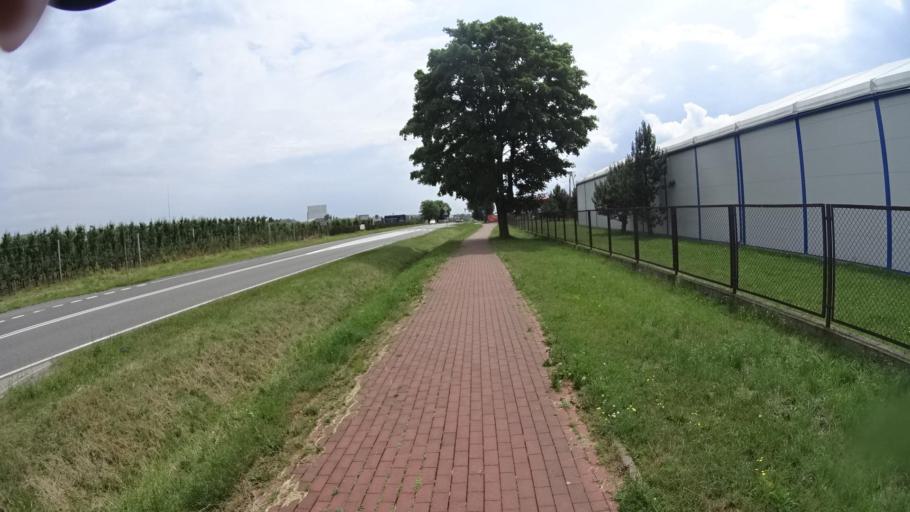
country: PL
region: Masovian Voivodeship
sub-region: Powiat grojecki
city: Grojec
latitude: 51.8843
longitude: 20.8633
